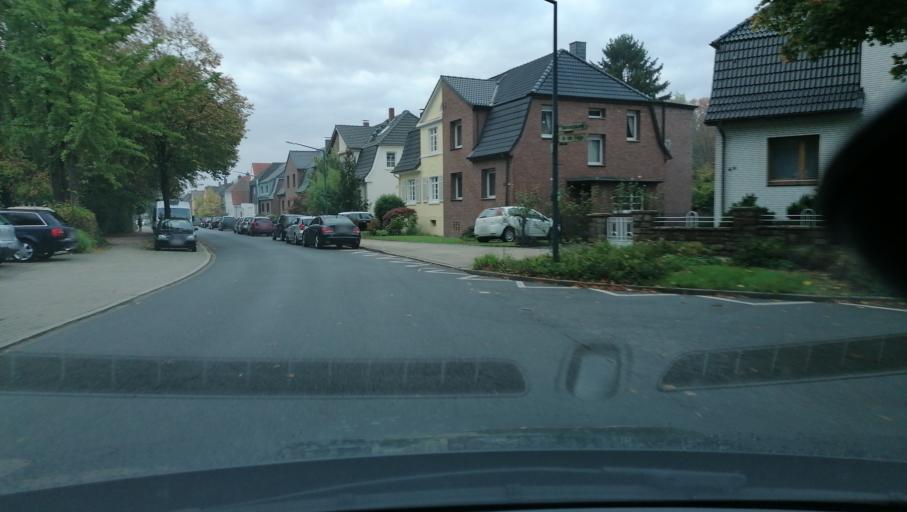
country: DE
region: North Rhine-Westphalia
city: Herten
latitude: 51.5896
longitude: 7.1359
